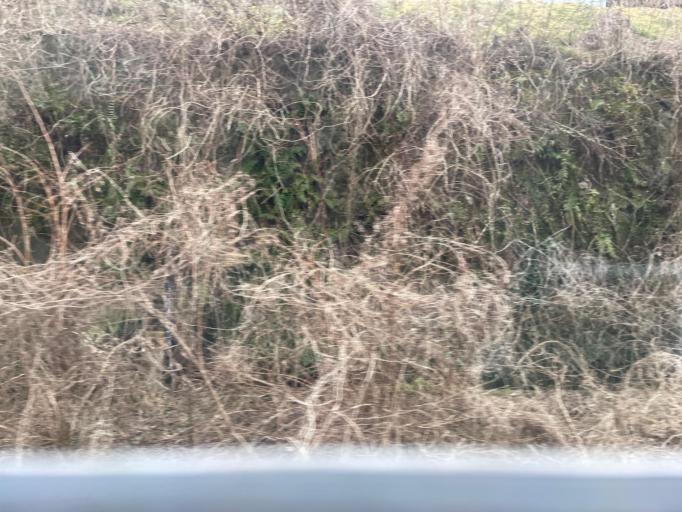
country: JP
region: Shizuoka
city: Gotemba
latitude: 35.3599
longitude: 138.9913
